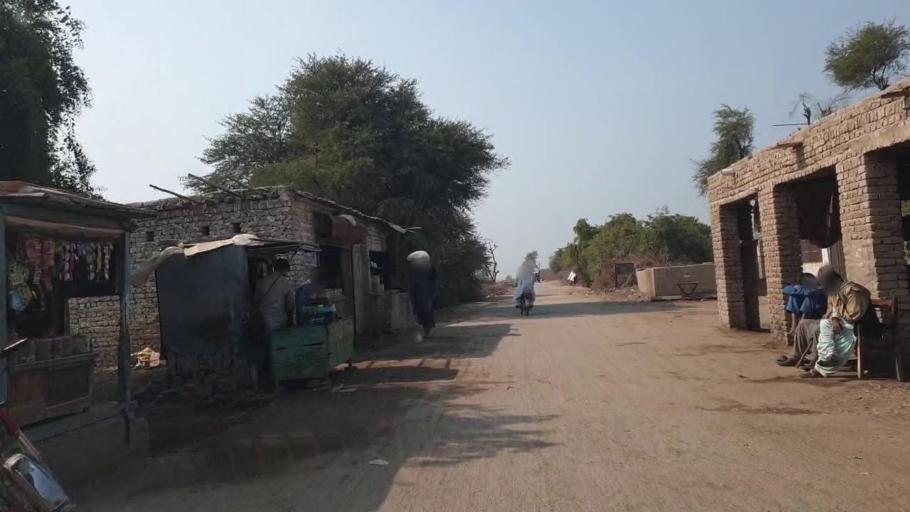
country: PK
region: Sindh
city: Hala
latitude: 25.8611
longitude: 68.4275
